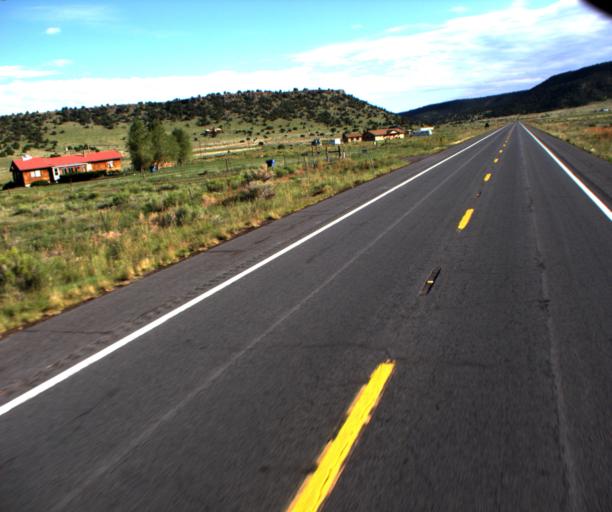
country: US
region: Arizona
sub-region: Apache County
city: Eagar
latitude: 34.0155
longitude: -109.1855
